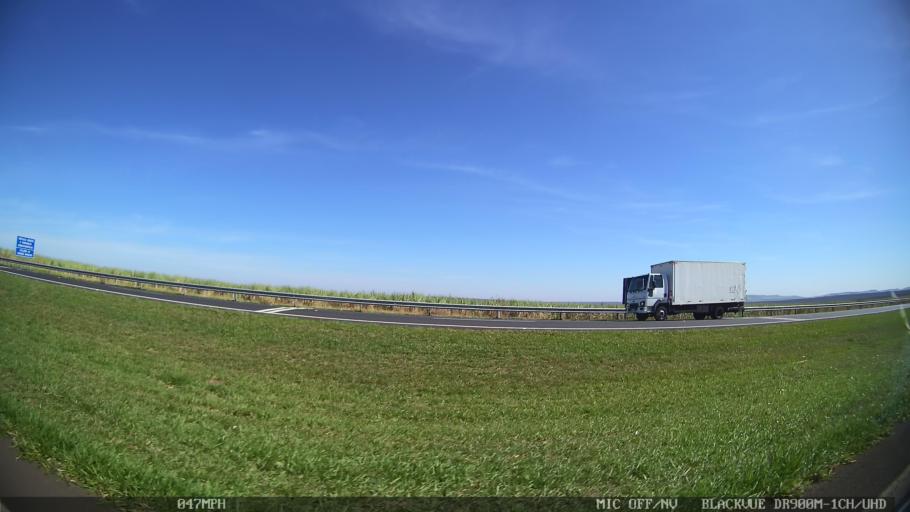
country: BR
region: Sao Paulo
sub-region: Santa Rita Do Passa Quatro
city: Santa Rita do Passa Quatro
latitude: -21.6547
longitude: -47.6096
